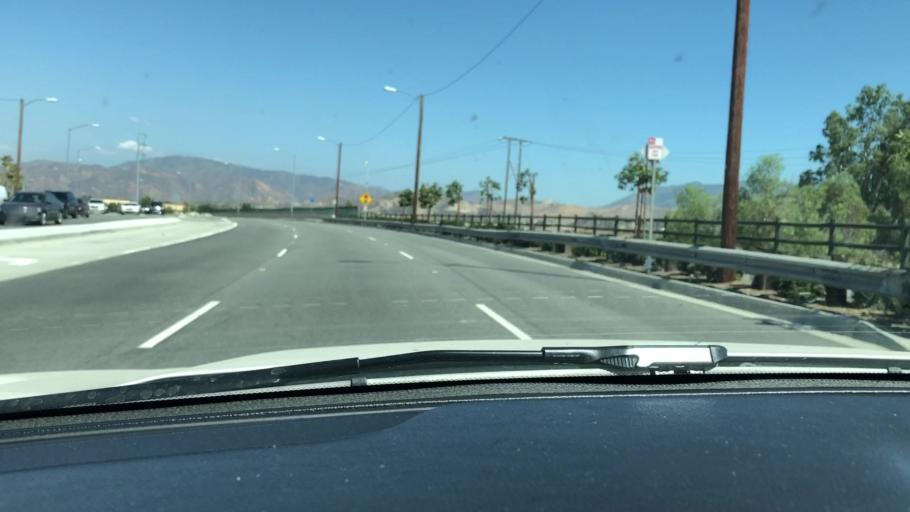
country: US
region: California
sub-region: Los Angeles County
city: Santa Clarita
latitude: 34.4161
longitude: -118.4794
